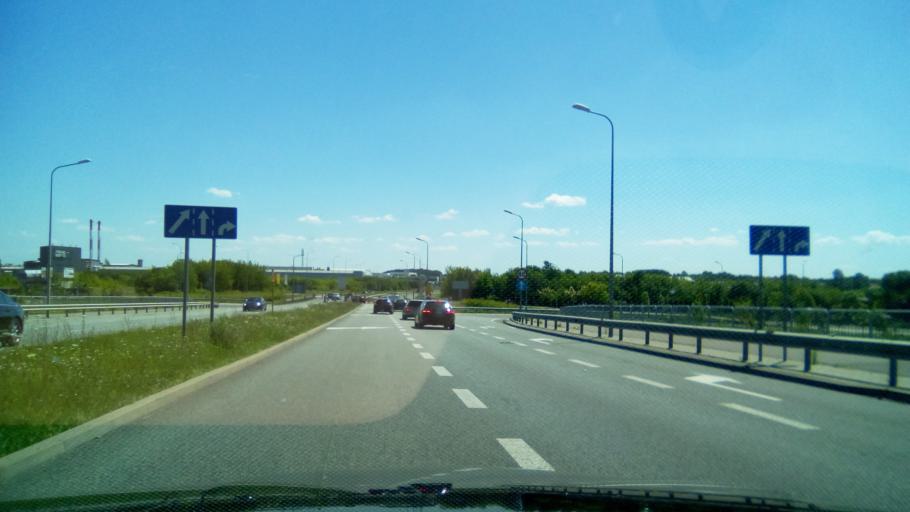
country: PL
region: Masovian Voivodeship
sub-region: Radom
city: Radom
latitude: 51.4193
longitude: 21.1876
